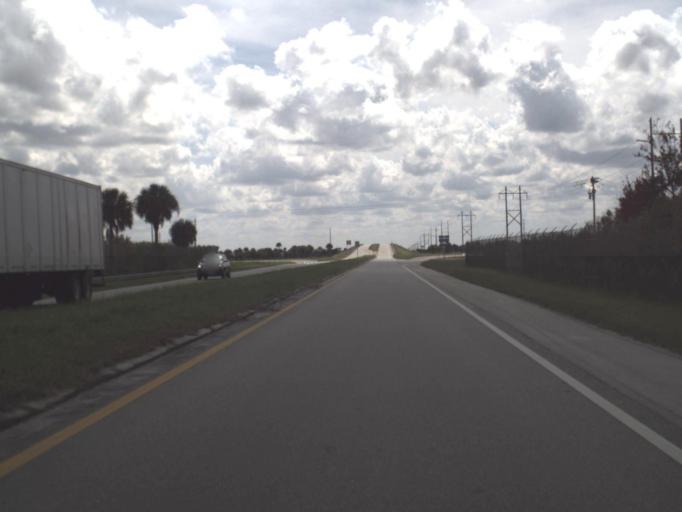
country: US
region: Florida
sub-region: Collier County
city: Immokalee
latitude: 26.1611
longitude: -81.3453
